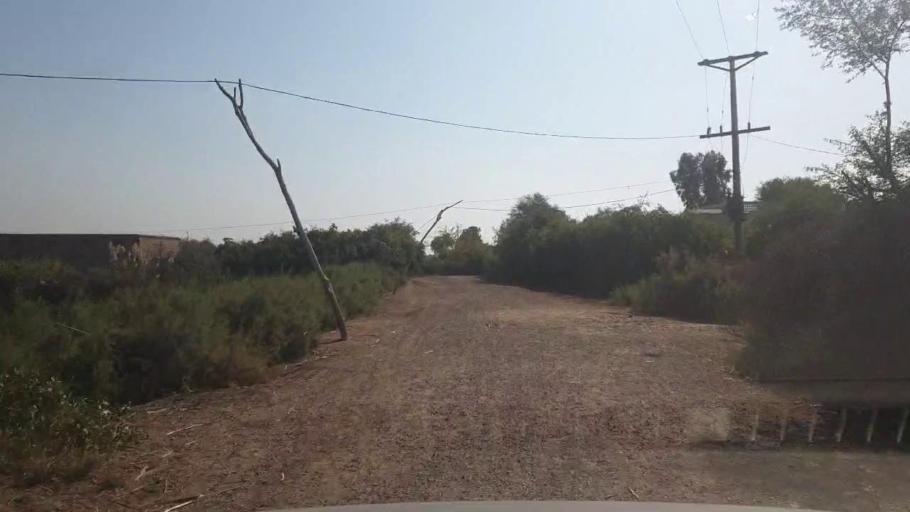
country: PK
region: Sindh
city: Chambar
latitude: 25.3193
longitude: 68.8655
